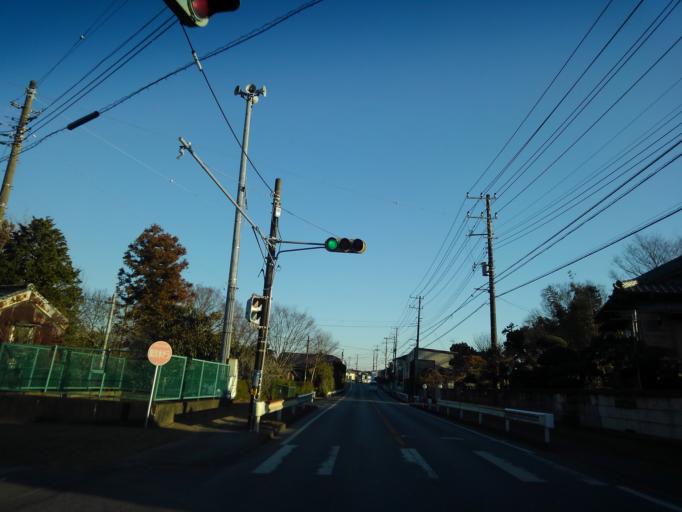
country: JP
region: Chiba
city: Kimitsu
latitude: 35.3105
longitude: 139.9378
